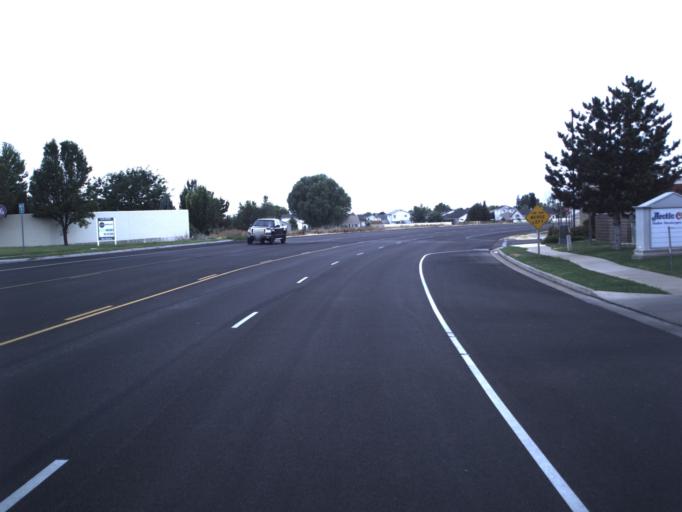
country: US
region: Utah
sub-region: Davis County
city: Clinton
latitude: 41.1617
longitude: -112.0656
